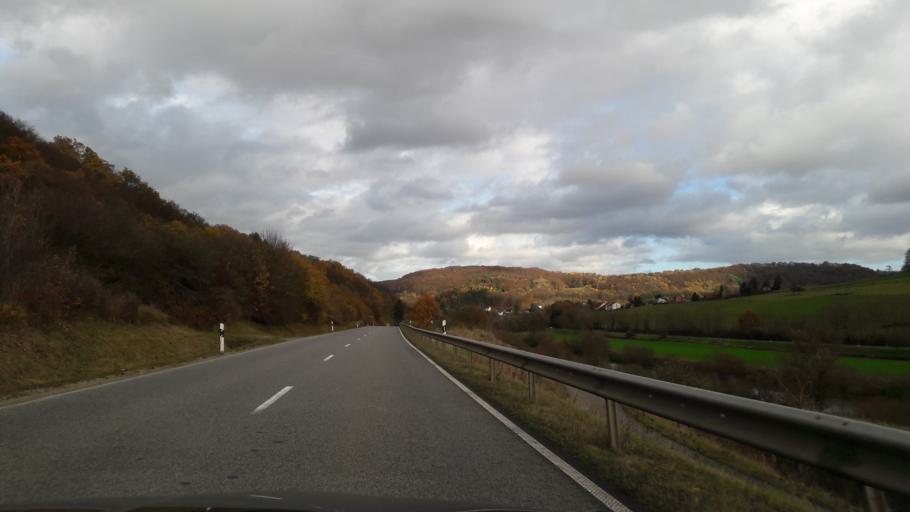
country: DE
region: Rheinland-Pfalz
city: Minden
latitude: 49.8159
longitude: 6.4580
